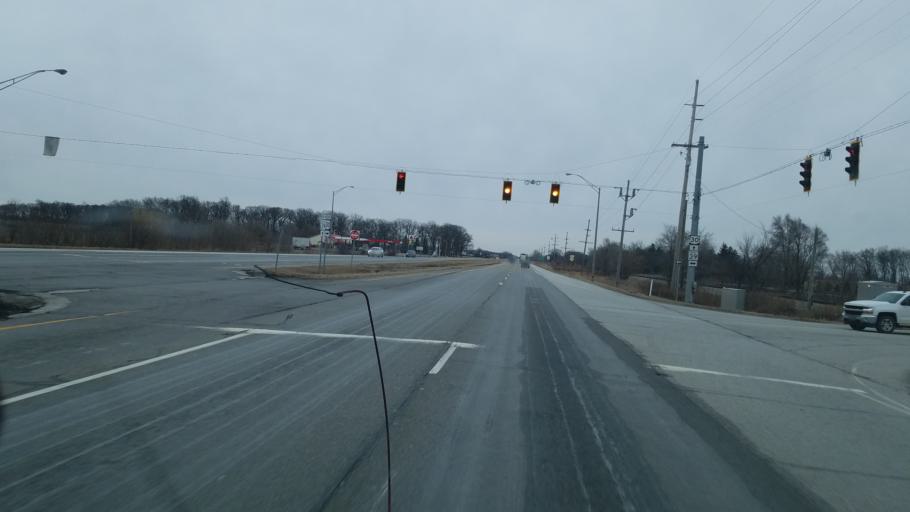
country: US
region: Indiana
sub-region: LaPorte County
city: Kingsford Heights
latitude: 41.4056
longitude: -86.7370
